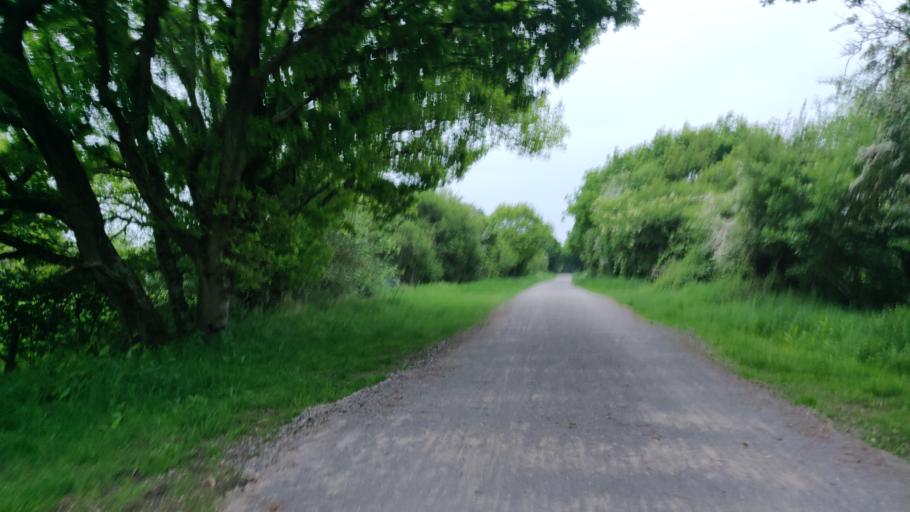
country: GB
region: England
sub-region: West Sussex
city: Partridge Green
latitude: 50.9718
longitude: -0.3157
